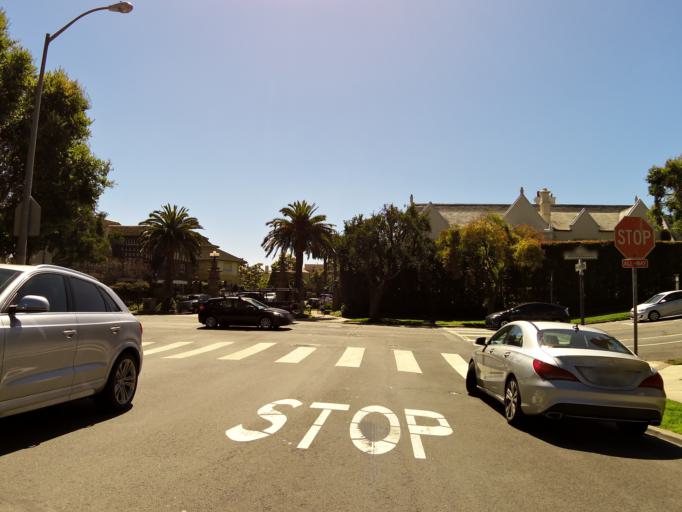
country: US
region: California
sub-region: San Francisco County
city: San Francisco
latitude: 37.7885
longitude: -122.4592
